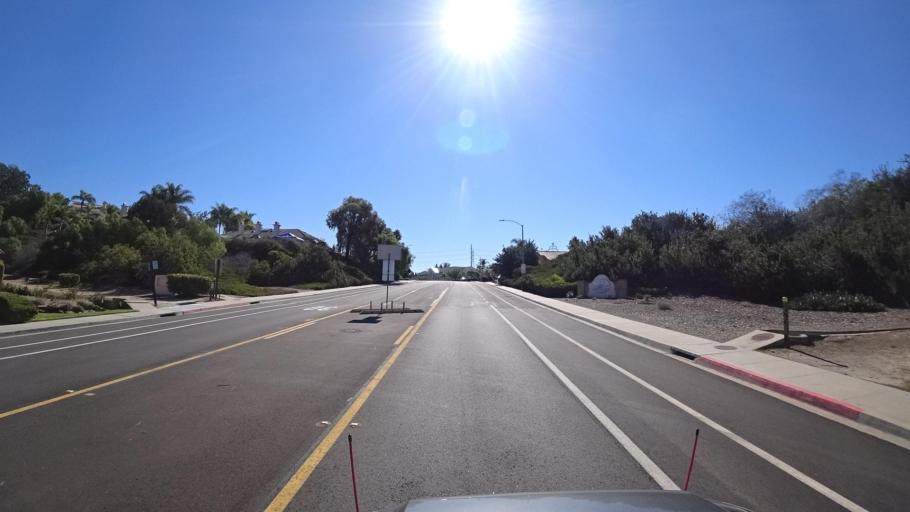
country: US
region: California
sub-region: San Diego County
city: Bonita
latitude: 32.6603
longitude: -116.9987
